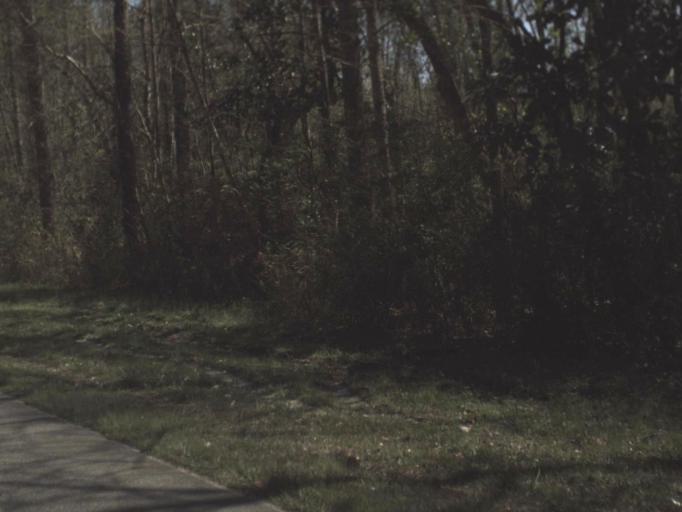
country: US
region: Florida
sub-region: Calhoun County
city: Blountstown
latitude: 30.4369
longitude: -85.1815
